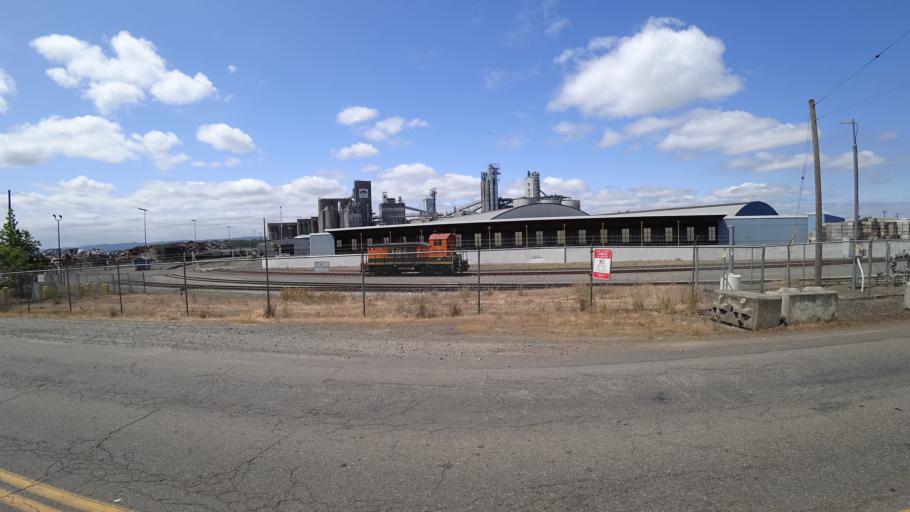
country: US
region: Washington
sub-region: Clark County
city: Vancouver
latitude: 45.6318
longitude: -122.6872
